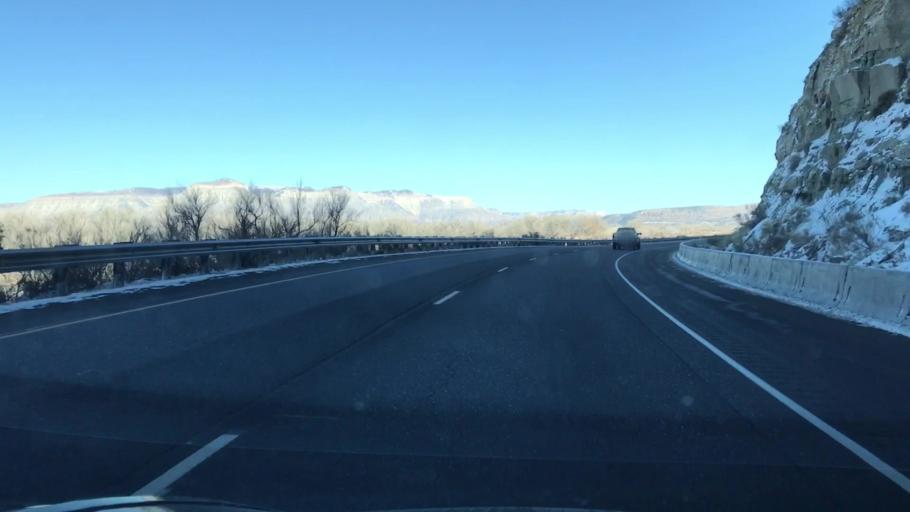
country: US
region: Colorado
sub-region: Mesa County
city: Palisade
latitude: 39.2769
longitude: -108.2415
